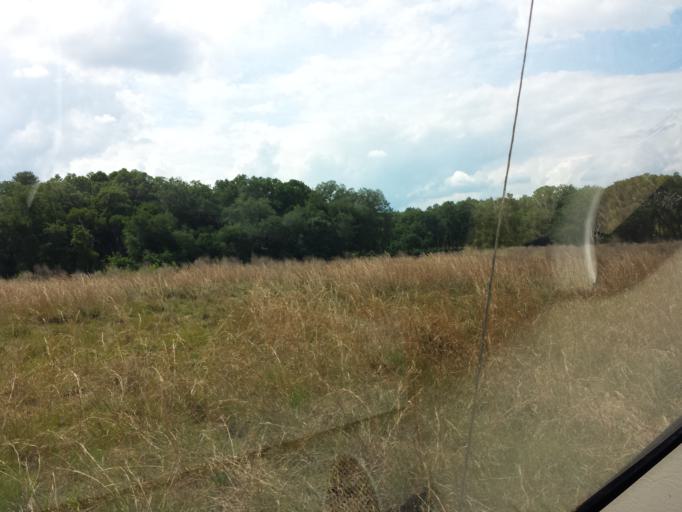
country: US
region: Florida
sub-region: Hernando County
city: Hill 'n Dale
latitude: 28.5509
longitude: -82.2585
